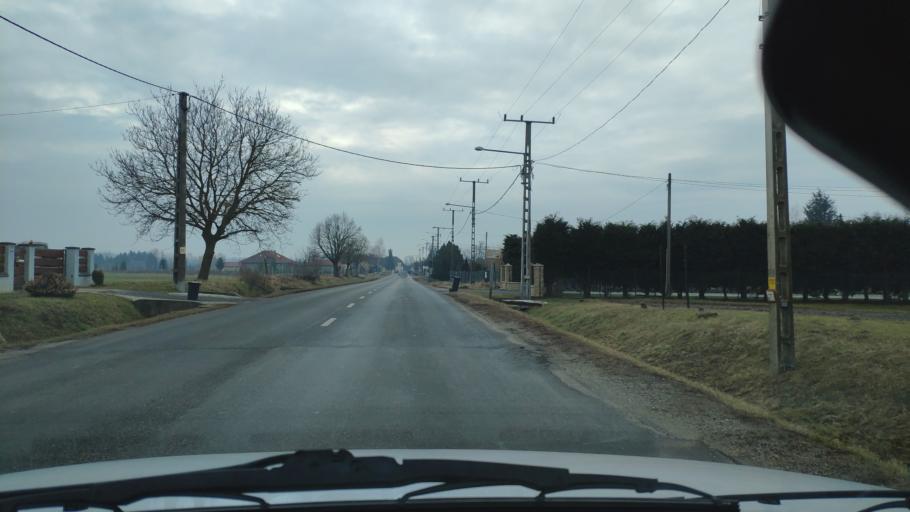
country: HU
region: Zala
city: Nagykanizsa
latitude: 46.5061
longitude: 16.9857
